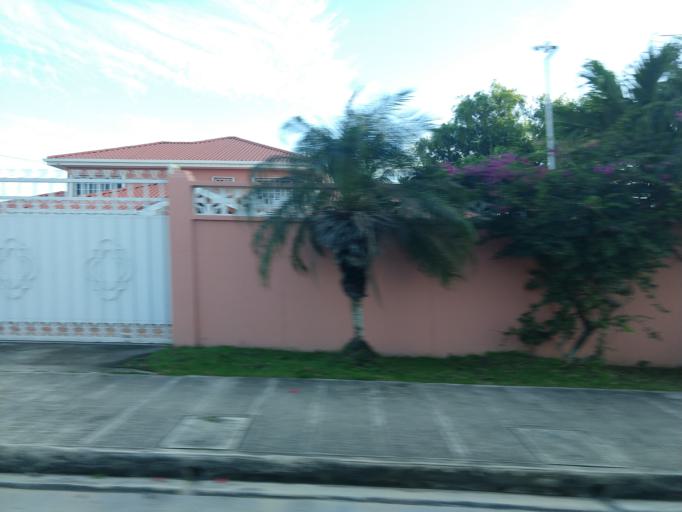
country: BZ
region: Belize
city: Belize City
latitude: 17.5120
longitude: -88.1928
